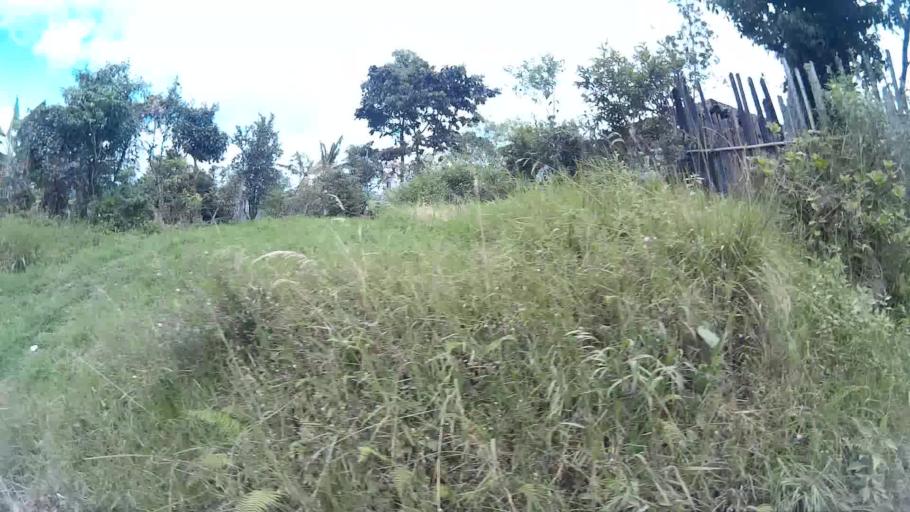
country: CO
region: Quindio
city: Filandia
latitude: 4.7134
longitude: -75.6468
